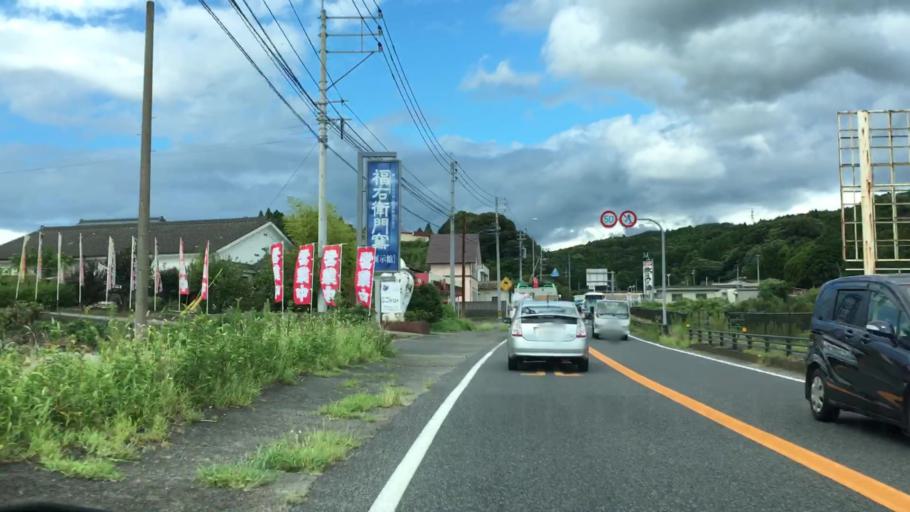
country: JP
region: Saga Prefecture
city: Imaricho-ko
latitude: 33.2842
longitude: 129.8989
